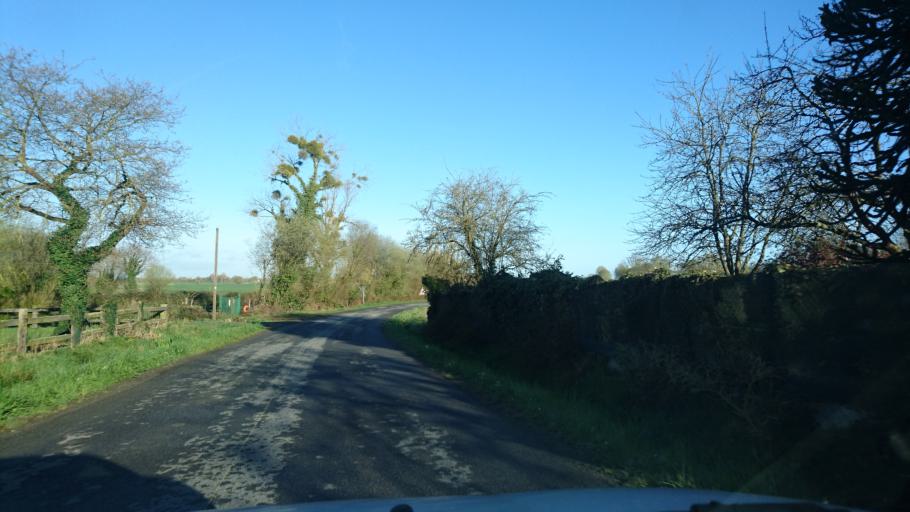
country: FR
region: Brittany
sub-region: Departement d'Ille-et-Vilaine
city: Baguer-Pican
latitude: 48.5711
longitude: -1.7024
